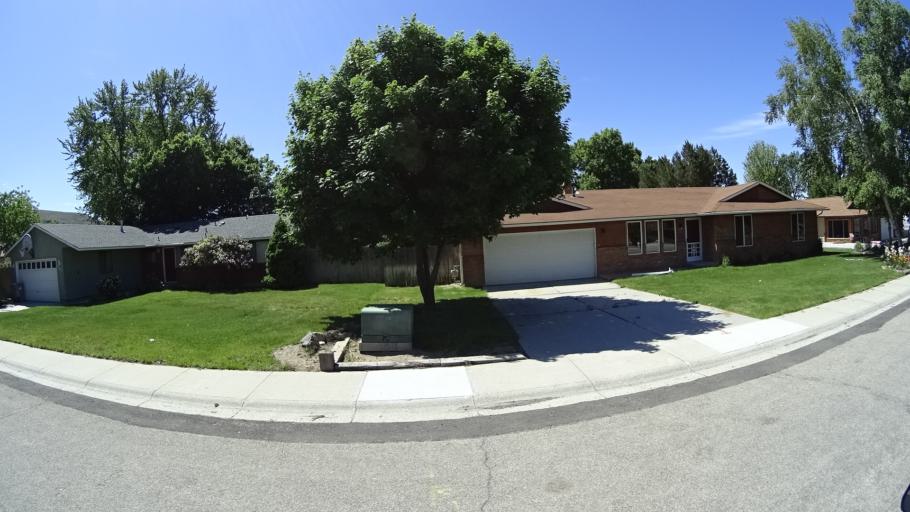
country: US
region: Idaho
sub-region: Ada County
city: Boise
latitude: 43.5599
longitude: -116.1005
